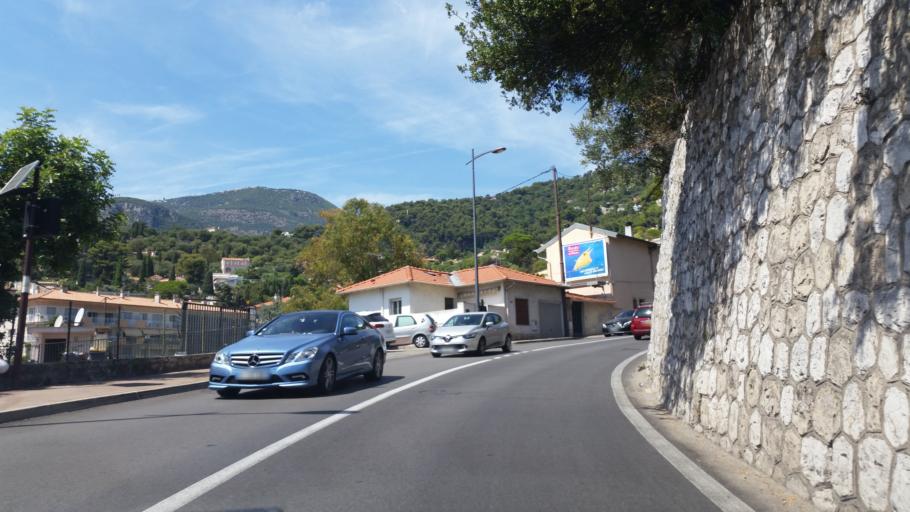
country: FR
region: Provence-Alpes-Cote d'Azur
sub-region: Departement des Alpes-Maritimes
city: Roquebrune-Cap-Martin
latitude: 43.7616
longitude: 7.4736
